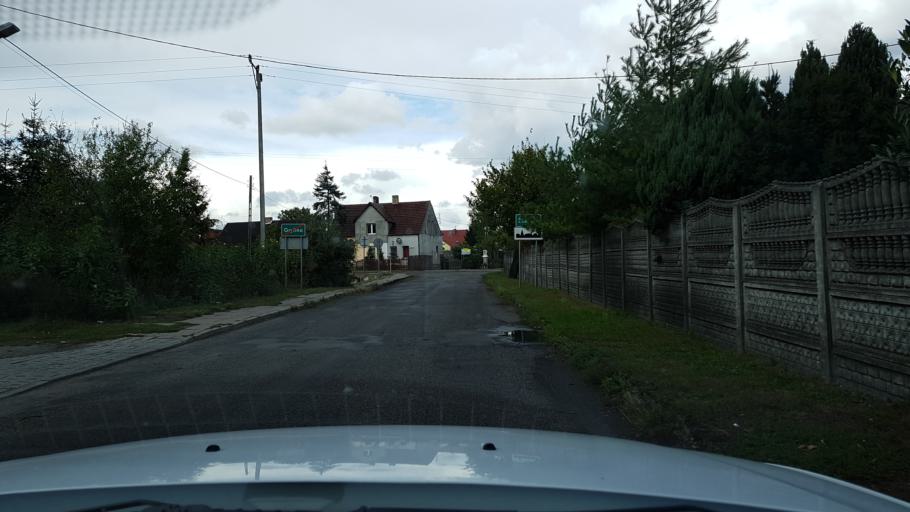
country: PL
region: West Pomeranian Voivodeship
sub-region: Powiat gryfinski
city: Gryfino
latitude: 53.2836
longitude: 14.5000
